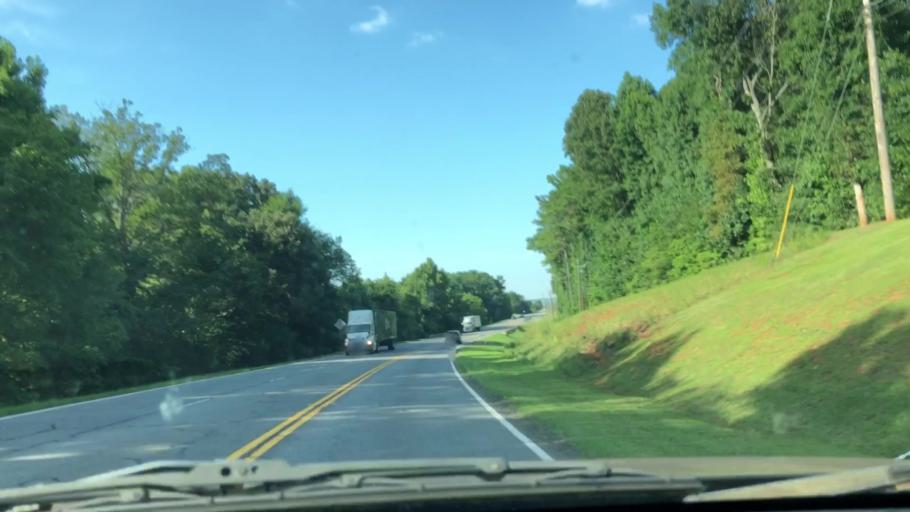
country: US
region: Georgia
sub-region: Bartow County
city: Rydal
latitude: 34.3080
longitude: -84.7286
